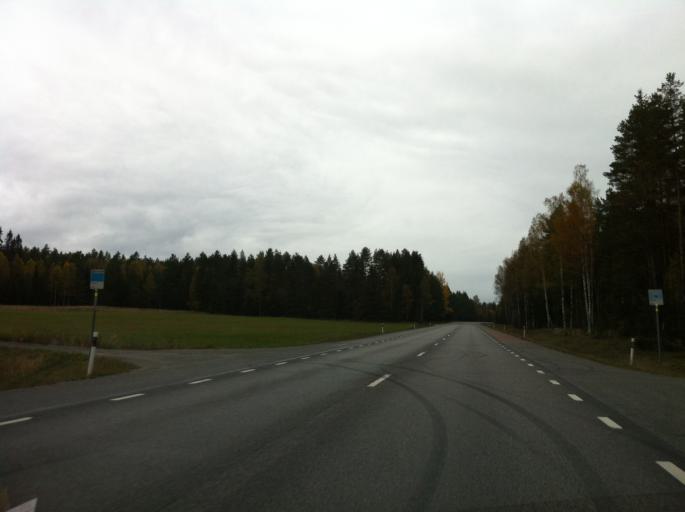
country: SE
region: OErebro
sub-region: Lindesbergs Kommun
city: Stora
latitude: 59.7666
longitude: 15.1484
